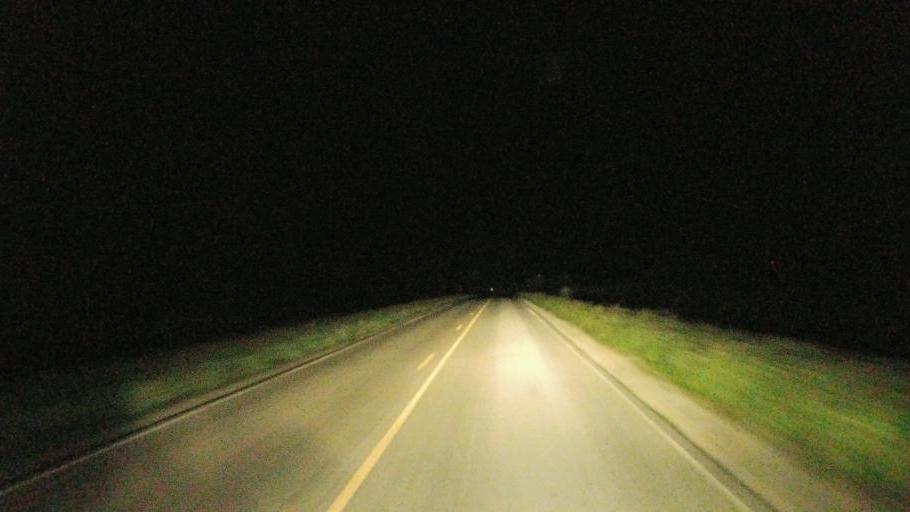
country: US
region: Iowa
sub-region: Decatur County
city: Lamoni
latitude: 40.6238
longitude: -93.9722
